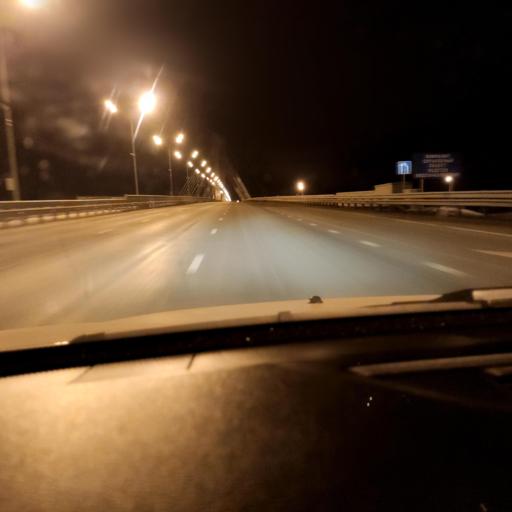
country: RU
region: Samara
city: Smyshlyayevka
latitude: 53.1830
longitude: 50.3044
